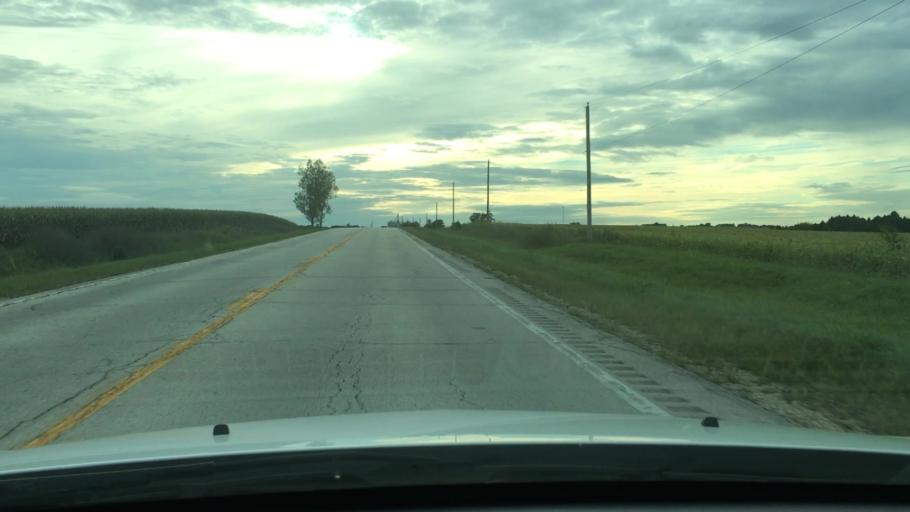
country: US
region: Illinois
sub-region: DeKalb County
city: Malta
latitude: 41.9355
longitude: -88.9263
